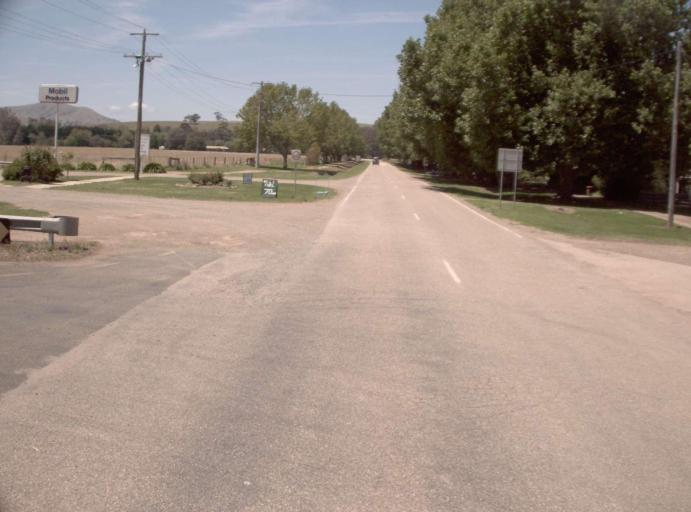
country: AU
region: Victoria
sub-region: East Gippsland
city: Bairnsdale
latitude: -37.2672
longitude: 147.7238
